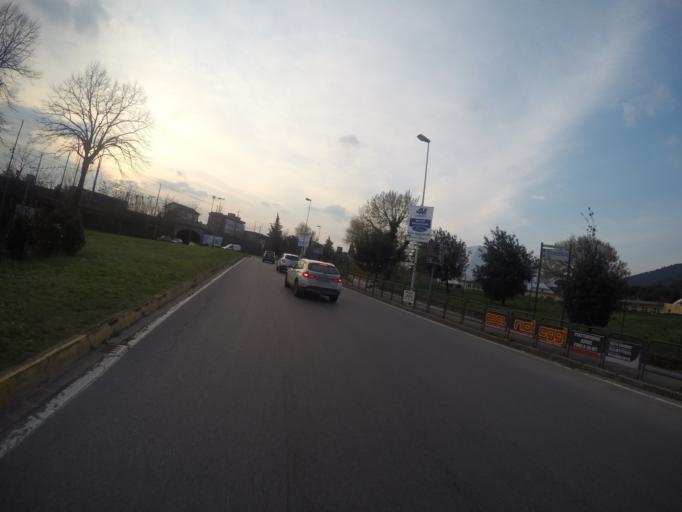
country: IT
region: Tuscany
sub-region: Provincia di Prato
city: Prato
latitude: 43.8728
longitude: 11.1185
